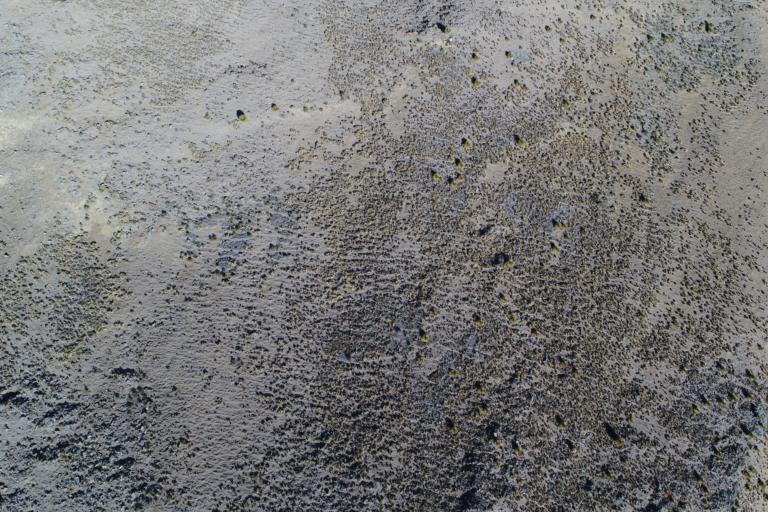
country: BO
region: La Paz
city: Viloco
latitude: -16.8123
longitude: -67.5475
